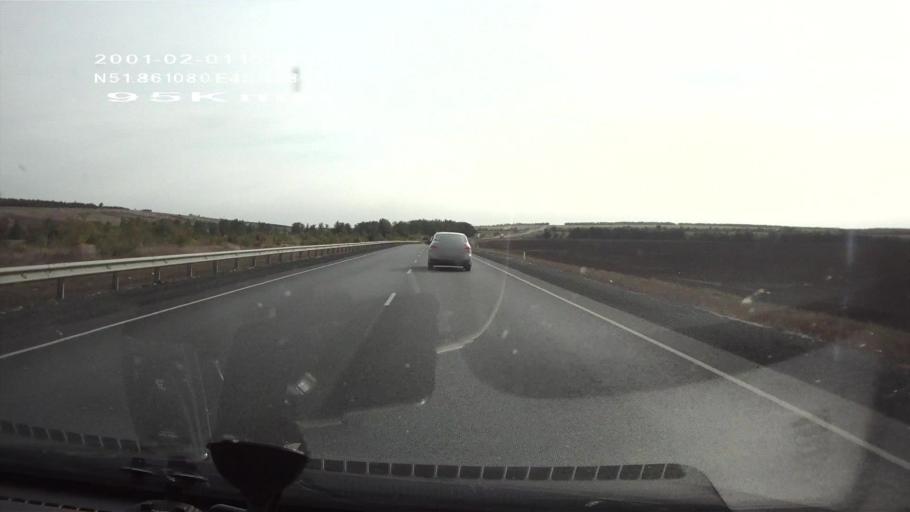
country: RU
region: Saratov
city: Yelshanka
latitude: 51.8643
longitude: 46.5005
